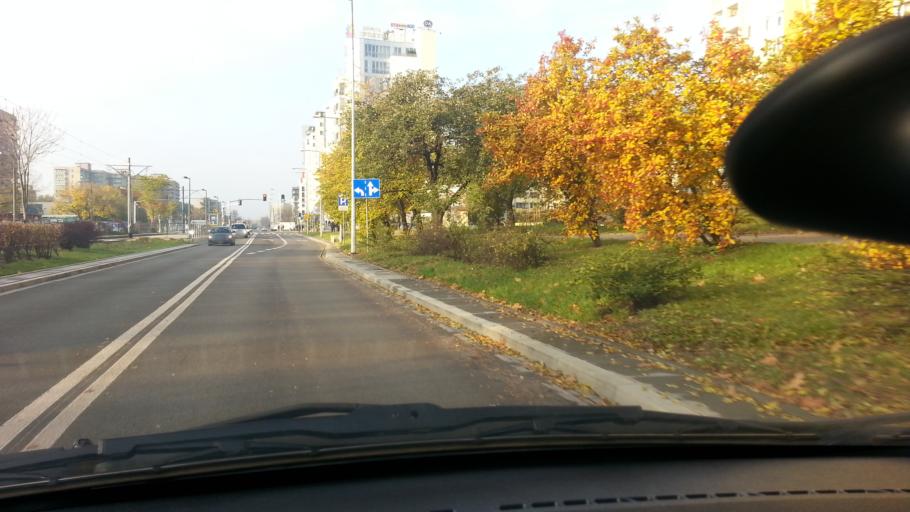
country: PL
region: Masovian Voivodeship
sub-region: Warszawa
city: Targowek
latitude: 52.2870
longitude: 21.0317
